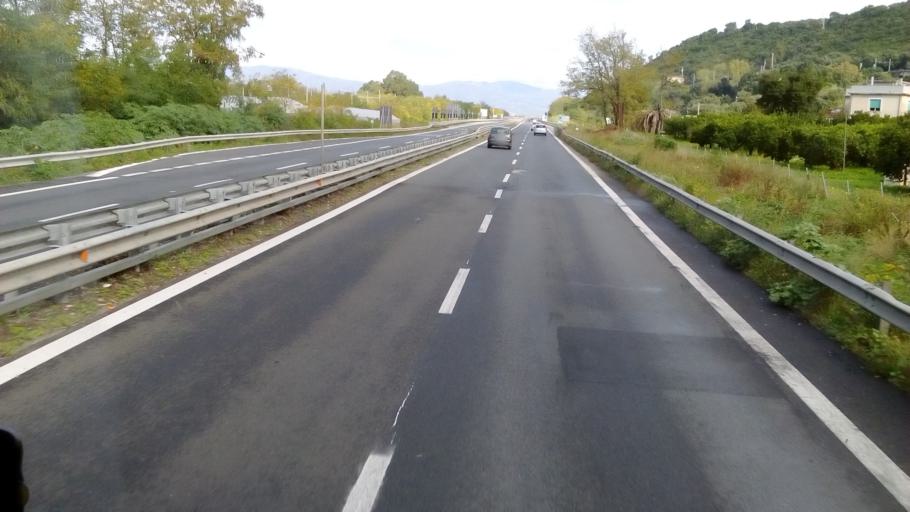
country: IT
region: Calabria
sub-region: Provincia di Vibo-Valentia
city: Pizzo
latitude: 38.7779
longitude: 16.2162
